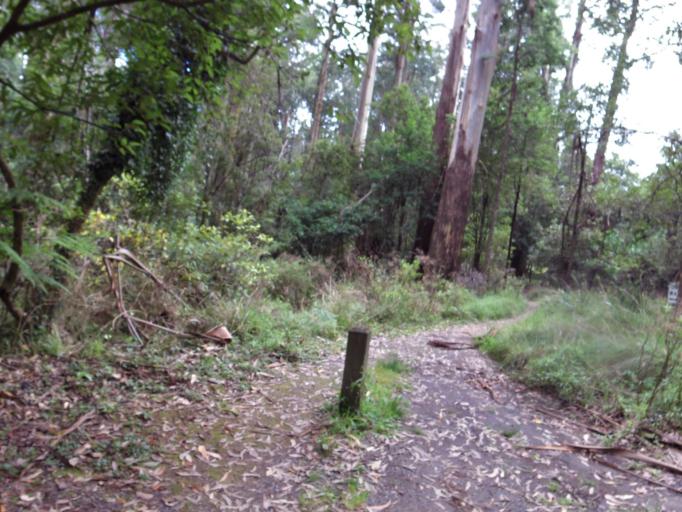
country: AU
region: Victoria
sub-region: Yarra Ranges
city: Kallista
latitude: -37.8809
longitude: 145.3591
